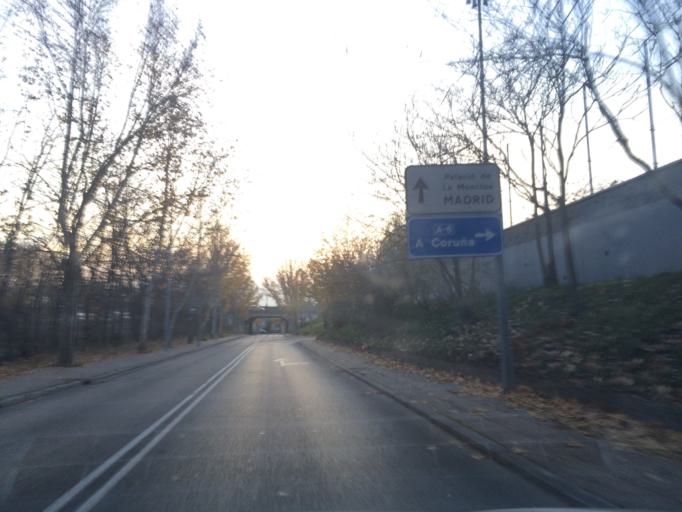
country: ES
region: Madrid
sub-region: Provincia de Madrid
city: Moncloa-Aravaca
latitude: 40.4458
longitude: -3.7312
